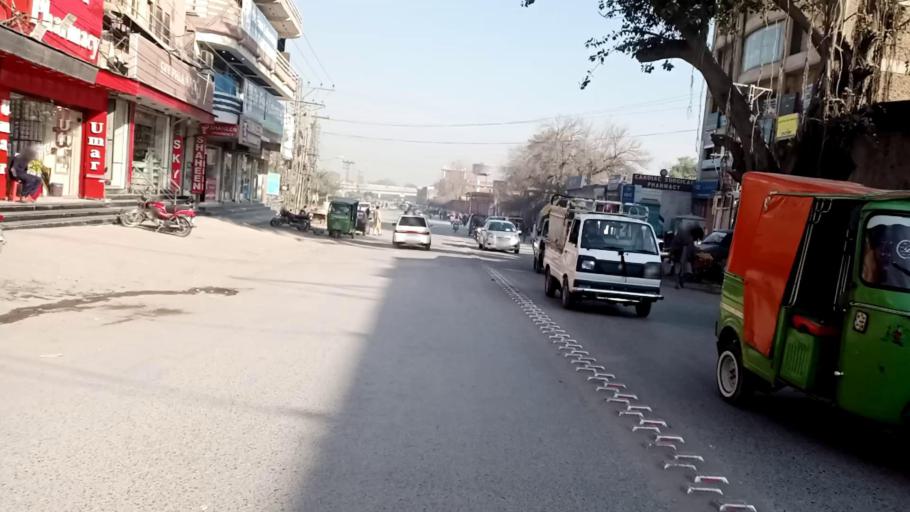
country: PK
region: Khyber Pakhtunkhwa
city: Peshawar
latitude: 34.0112
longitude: 71.5715
